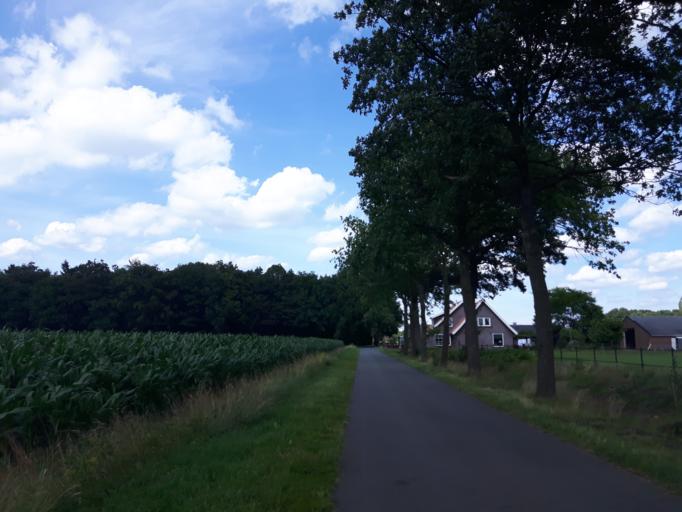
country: NL
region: Overijssel
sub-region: Gemeente Haaksbergen
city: Haaksbergen
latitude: 52.1828
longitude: 6.7642
